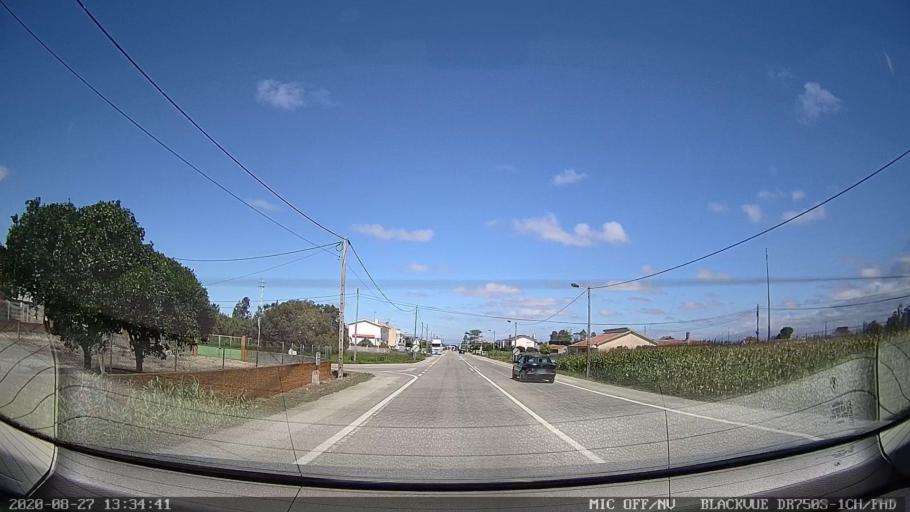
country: PT
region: Coimbra
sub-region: Mira
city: Mira
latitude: 40.4697
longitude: -8.6982
